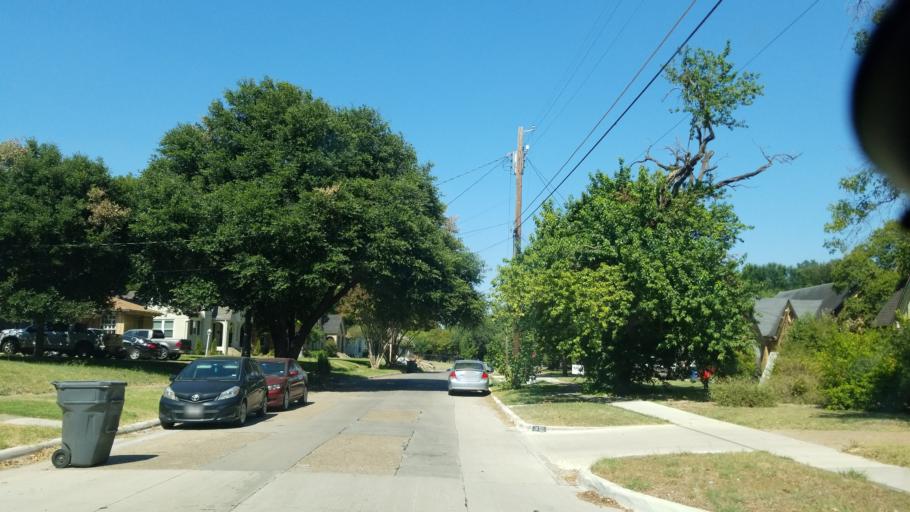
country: US
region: Texas
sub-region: Dallas County
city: Cockrell Hill
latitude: 32.7304
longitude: -96.8459
